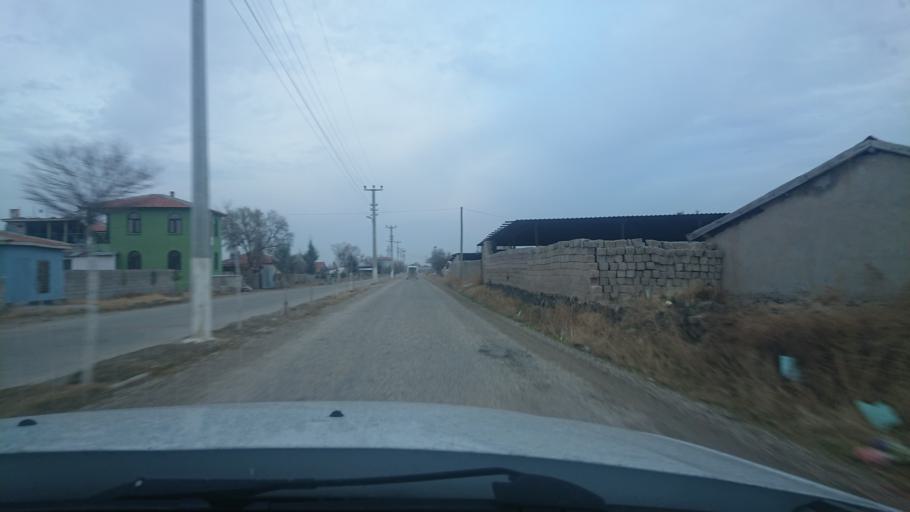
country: TR
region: Aksaray
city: Yesilova
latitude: 38.4158
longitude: 33.8369
